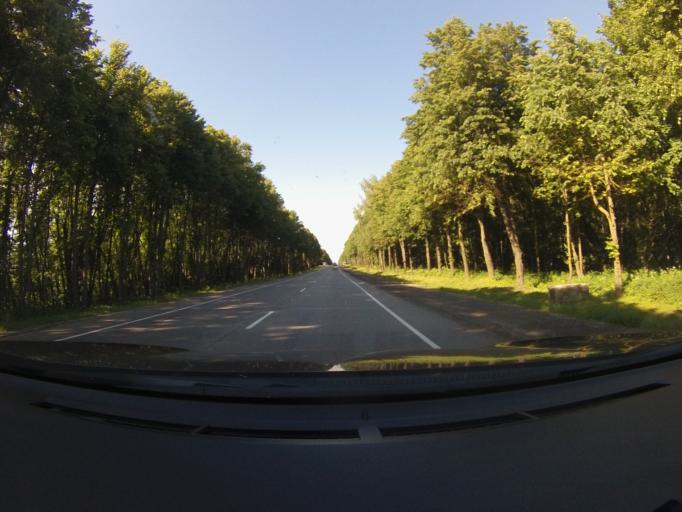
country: RU
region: Orjol
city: Spasskoye-Lutovinovo
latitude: 53.3516
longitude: 36.7158
